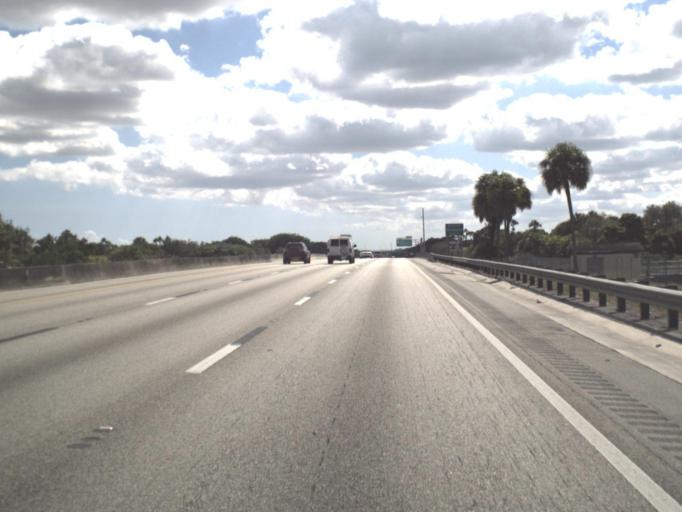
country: US
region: Florida
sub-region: Palm Beach County
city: Boca Pointe
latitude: 26.3292
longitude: -80.1704
